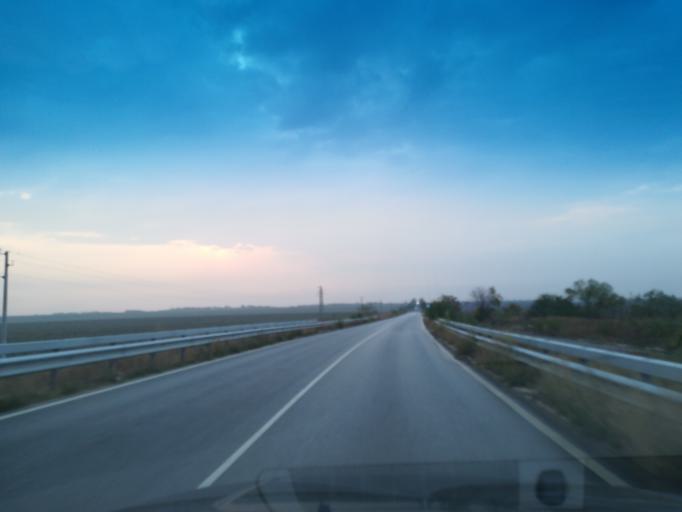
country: BG
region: Stara Zagora
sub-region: Obshtina Chirpan
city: Chirpan
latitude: 42.1810
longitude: 25.2449
